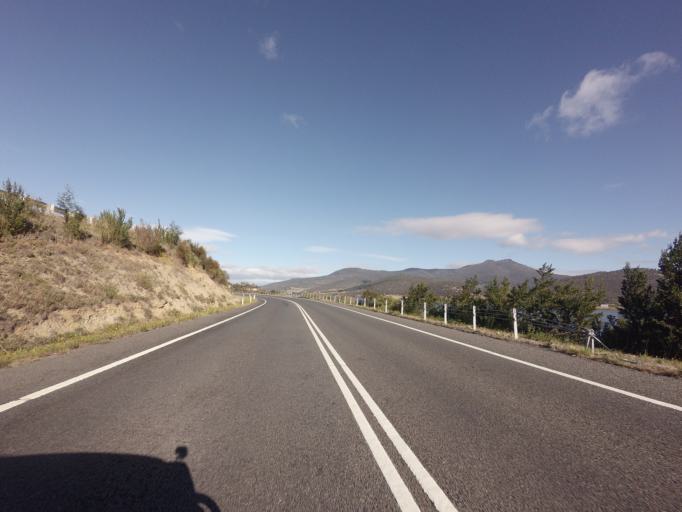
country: AU
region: Tasmania
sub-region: Brighton
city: Bridgewater
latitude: -42.7411
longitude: 147.1958
